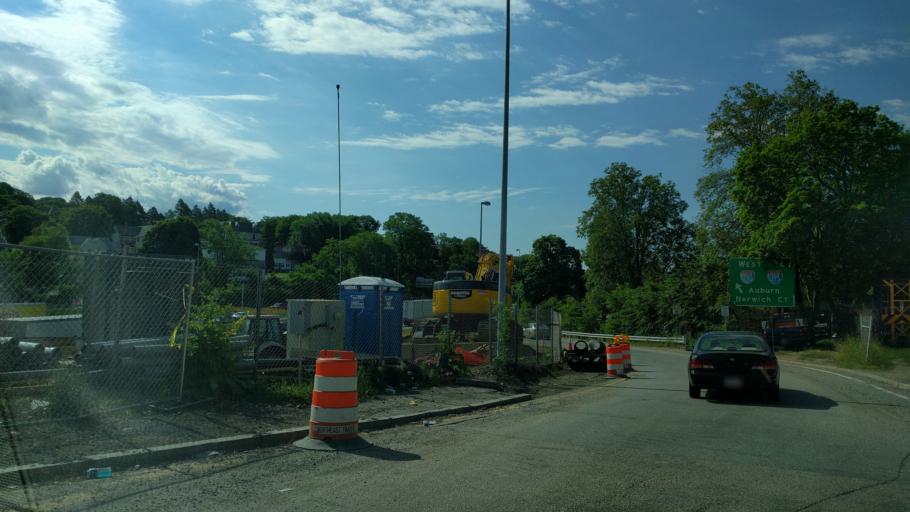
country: US
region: Massachusetts
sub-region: Worcester County
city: Worcester
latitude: 42.2716
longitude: -71.7953
